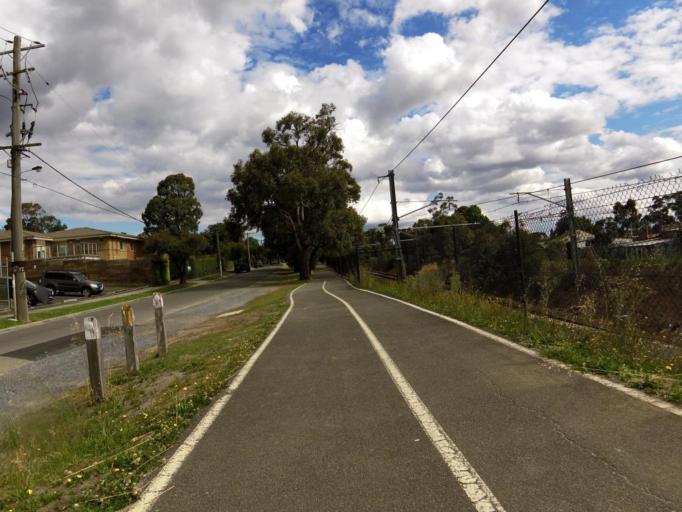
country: AU
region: Victoria
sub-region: Knox
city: Boronia
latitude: -37.8636
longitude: 145.2862
